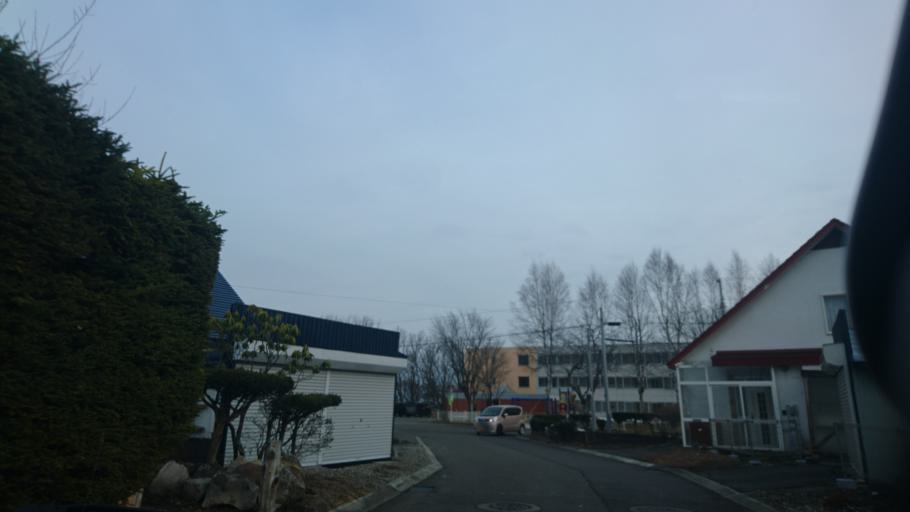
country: JP
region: Hokkaido
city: Otofuke
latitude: 42.9985
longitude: 143.1941
